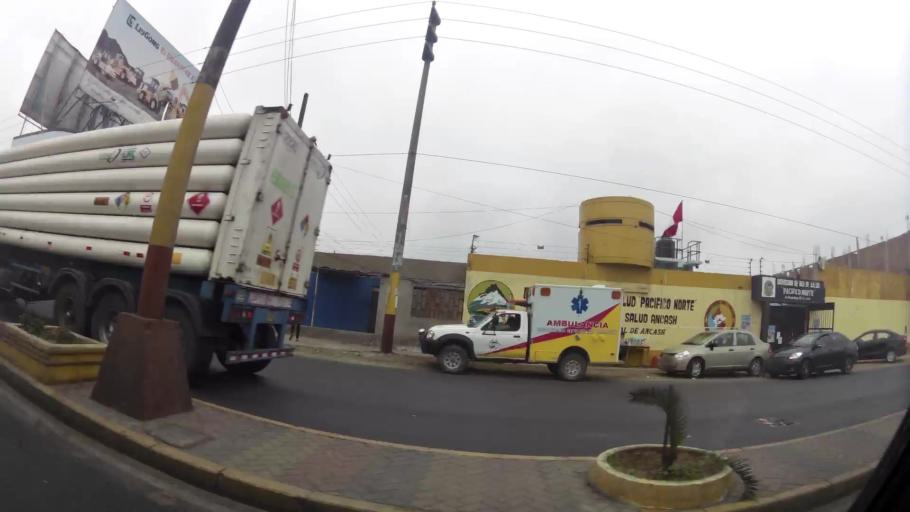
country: PE
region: Ancash
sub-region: Provincia de Santa
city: Chimbote
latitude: -9.0812
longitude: -78.5803
